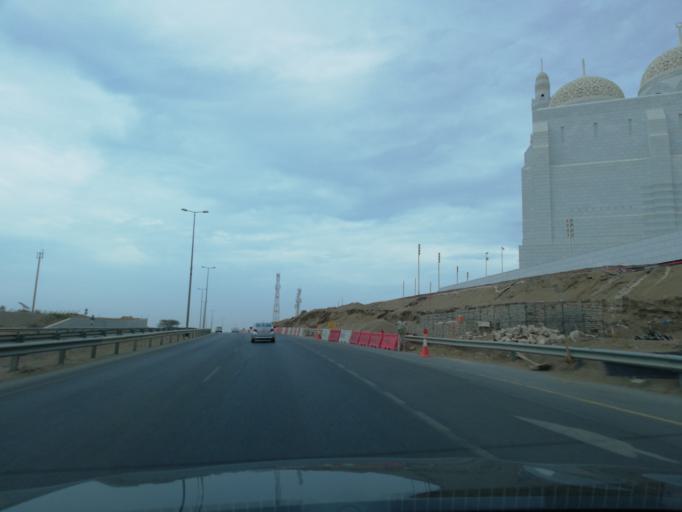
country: OM
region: Muhafazat Masqat
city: Bawshar
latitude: 23.5787
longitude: 58.4130
